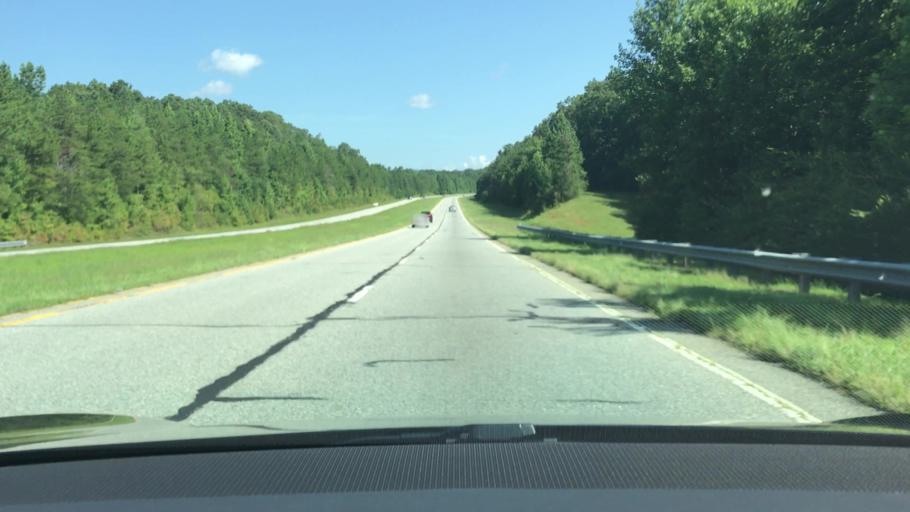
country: US
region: Georgia
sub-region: Habersham County
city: Clarkesville
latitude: 34.6328
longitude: -83.4492
